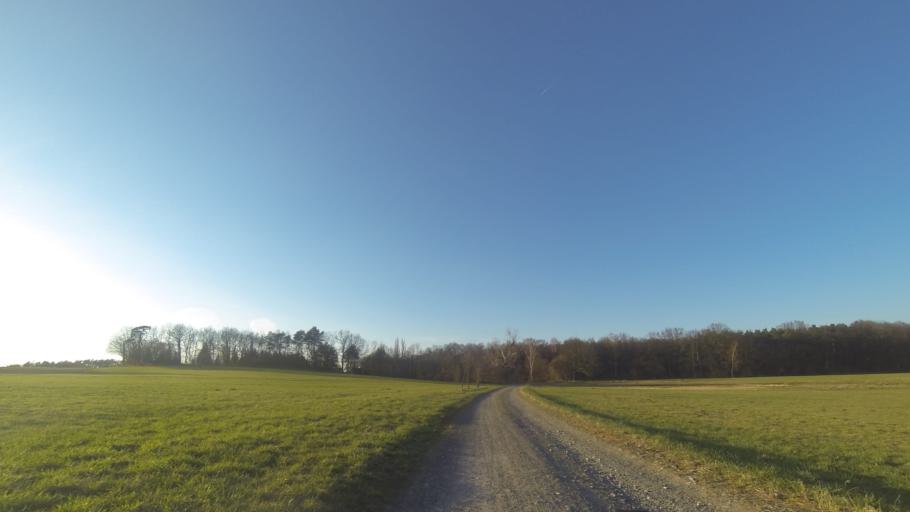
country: DE
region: Saxony
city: Albertstadt
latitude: 51.1356
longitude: 13.7590
